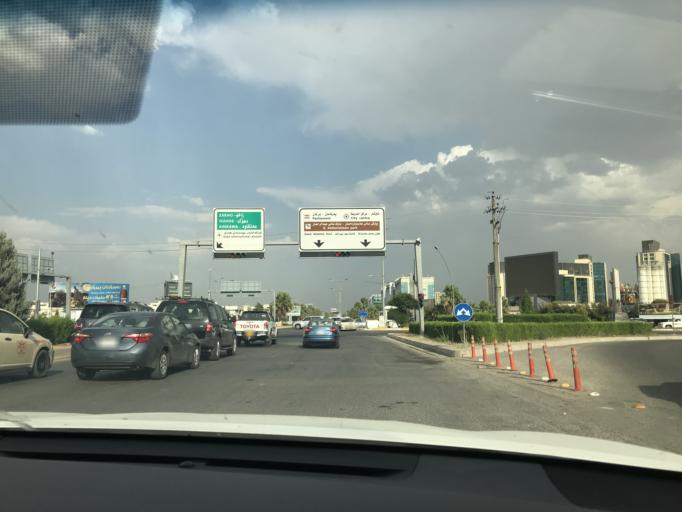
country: IQ
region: Arbil
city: Erbil
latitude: 36.2046
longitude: 43.9664
